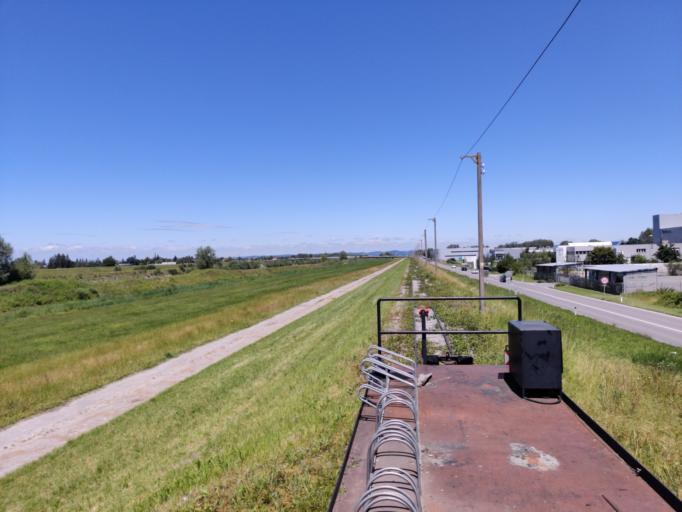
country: AT
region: Vorarlberg
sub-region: Politischer Bezirk Bregenz
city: Fussach
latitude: 47.4696
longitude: 9.6707
